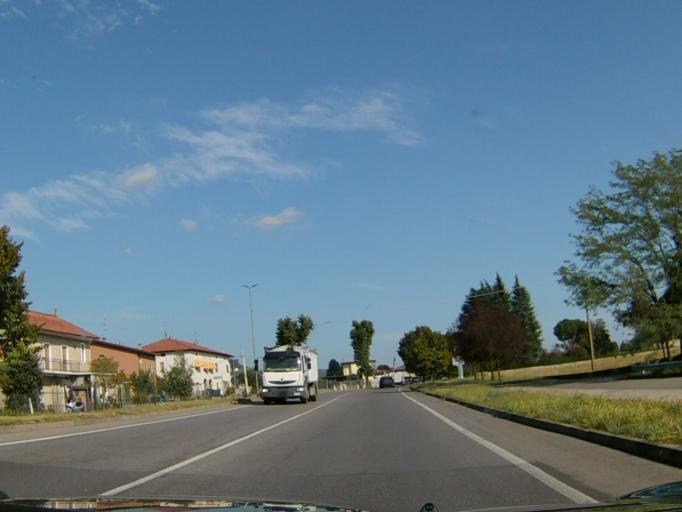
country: IT
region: Lombardy
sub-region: Provincia di Brescia
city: Palazzolo sull'Oglio
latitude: 45.5901
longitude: 9.9020
